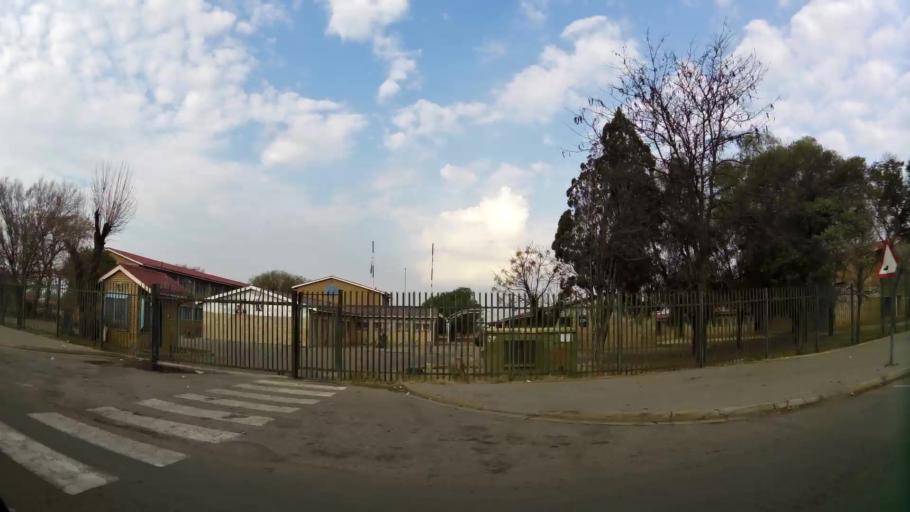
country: ZA
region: Gauteng
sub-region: Sedibeng District Municipality
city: Vanderbijlpark
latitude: -26.6903
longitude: 27.8674
